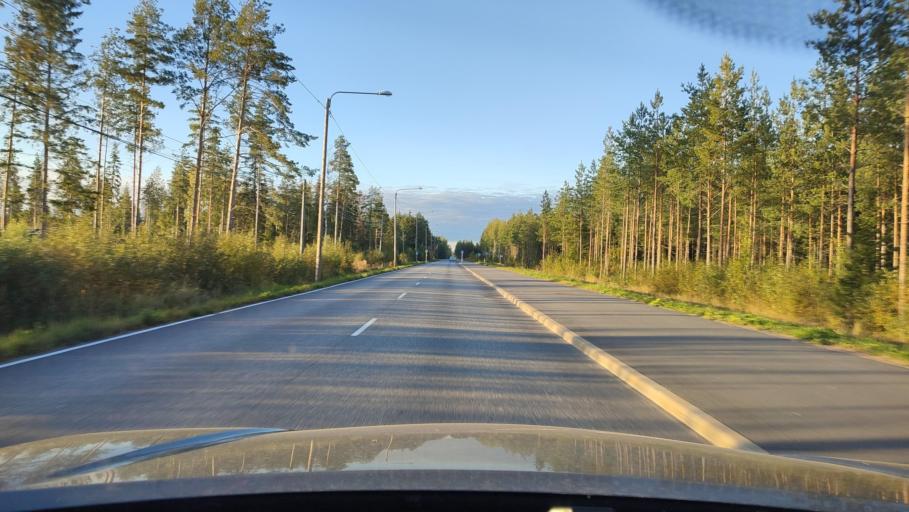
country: FI
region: Ostrobothnia
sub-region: Sydosterbotten
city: Kristinestad
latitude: 62.2323
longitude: 21.5210
